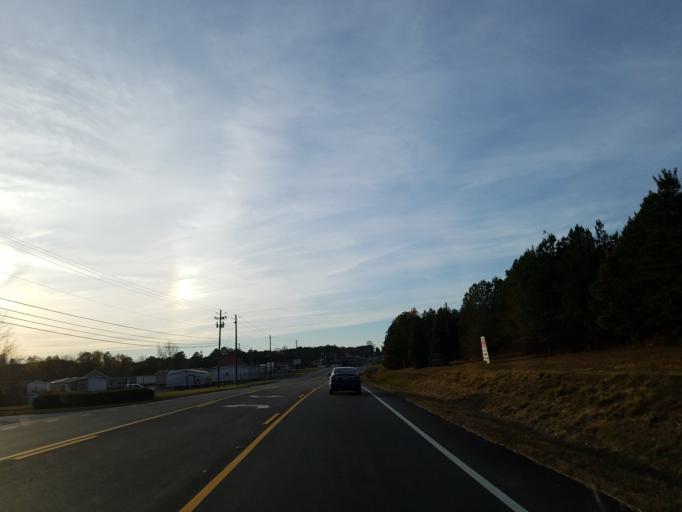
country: US
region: Georgia
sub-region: Haralson County
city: Bremen
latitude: 33.7218
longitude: -85.1200
